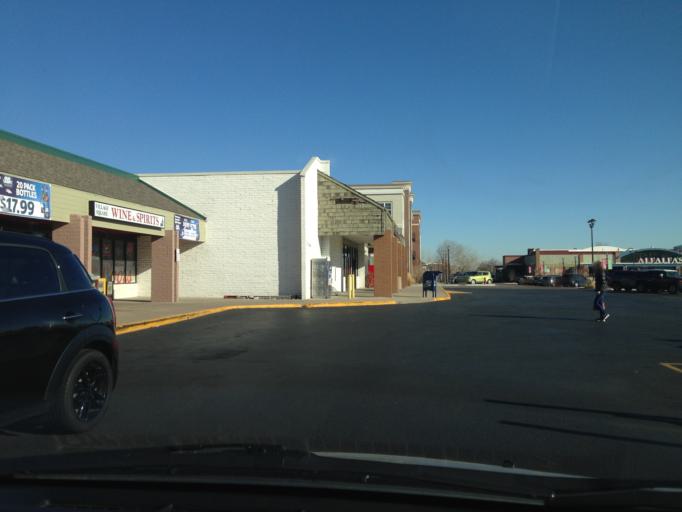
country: US
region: Colorado
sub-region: Boulder County
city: Louisville
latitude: 39.9879
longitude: -105.1358
